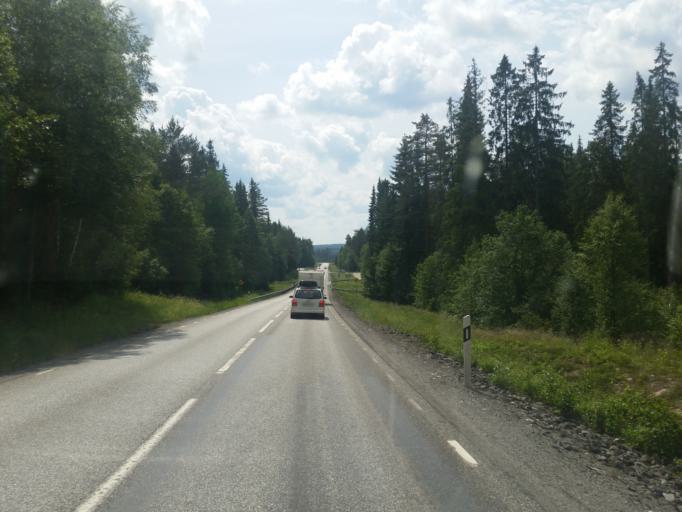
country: SE
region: OErebro
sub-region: Ljusnarsbergs Kommun
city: Kopparberg
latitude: 59.9044
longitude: 15.0207
